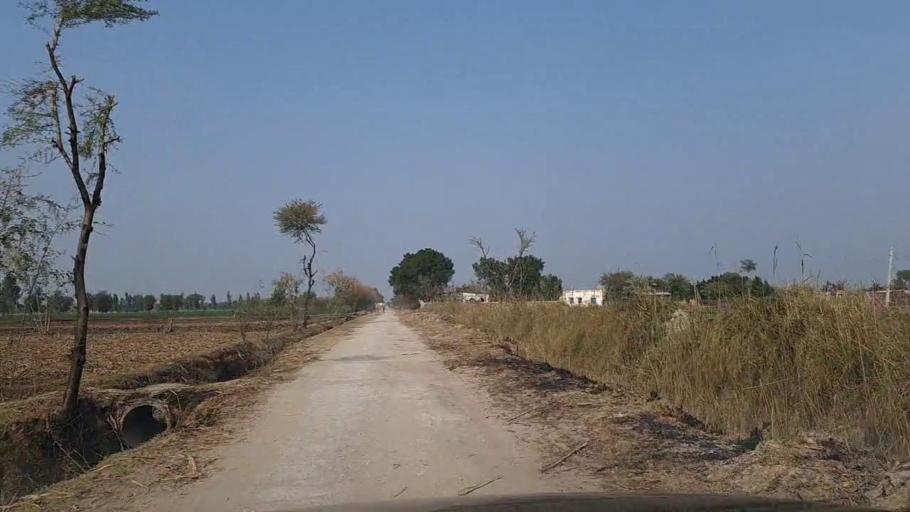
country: PK
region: Sindh
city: Daur
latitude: 26.3969
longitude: 68.4238
